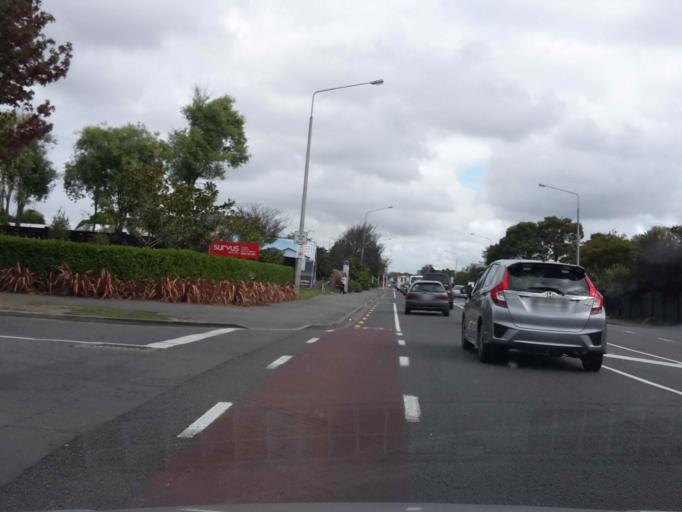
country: NZ
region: Canterbury
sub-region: Christchurch City
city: Christchurch
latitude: -43.4890
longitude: 172.6150
